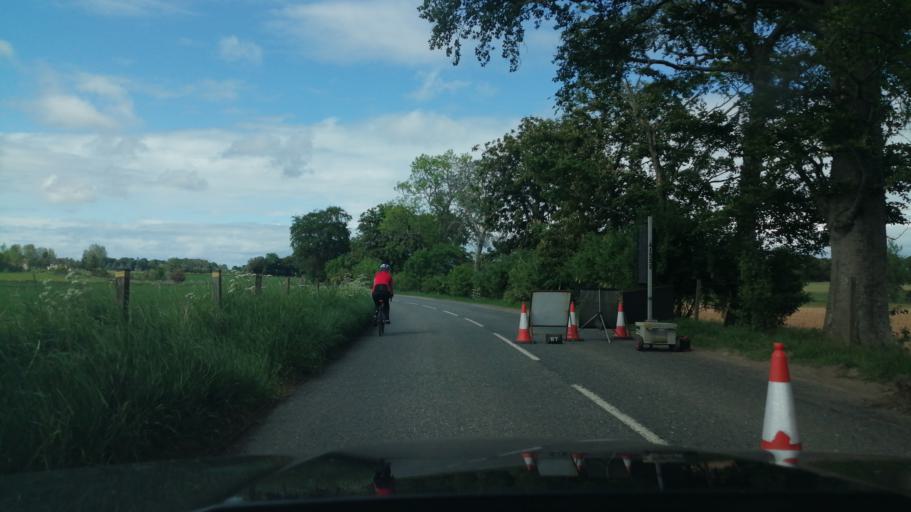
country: GB
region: Scotland
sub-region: Moray
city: Lhanbryd
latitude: 57.6436
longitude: -3.2473
